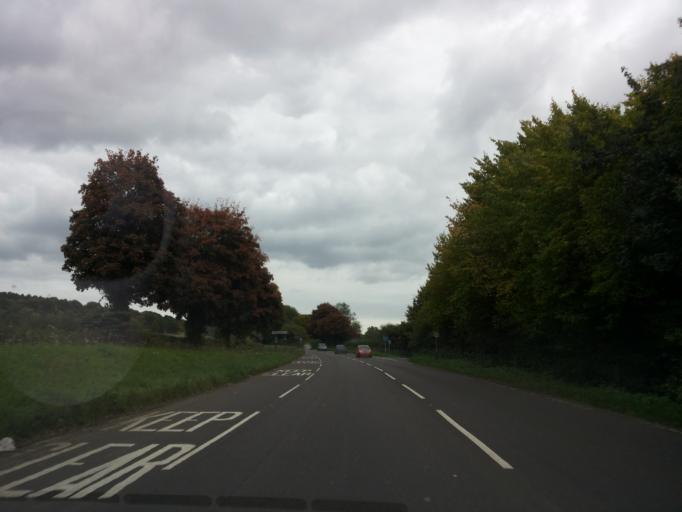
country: GB
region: England
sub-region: Buckinghamshire
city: Great Missenden
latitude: 51.6848
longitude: -0.6796
